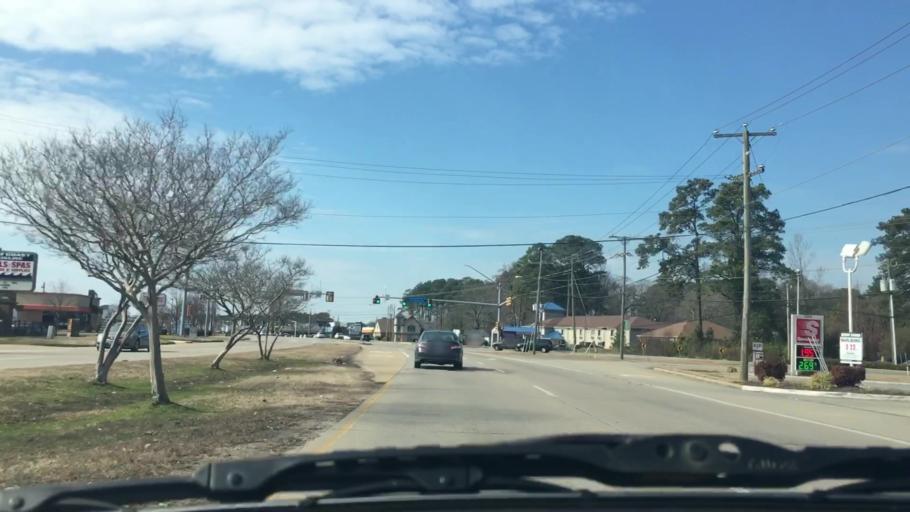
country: US
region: Virginia
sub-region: City of Portsmouth
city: Portsmouth Heights
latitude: 36.8651
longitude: -76.4090
